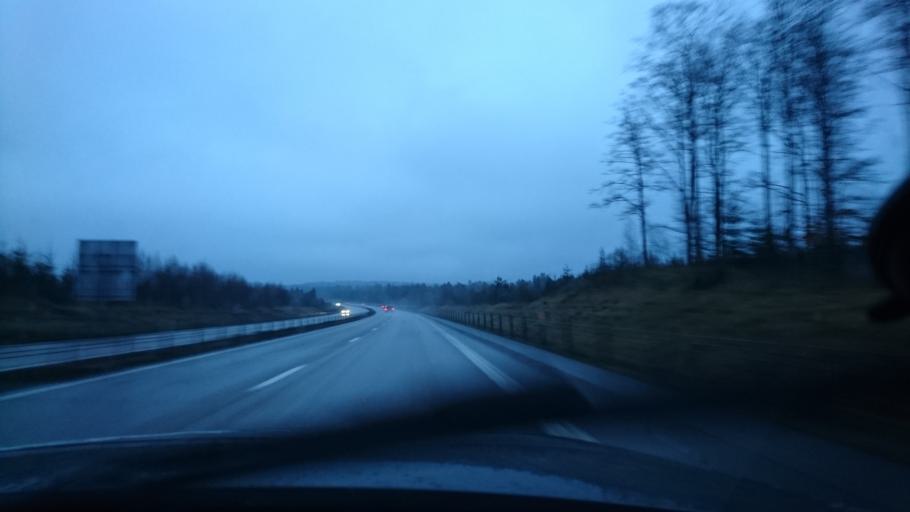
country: SE
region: Skane
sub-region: Orkelljunga Kommun
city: OErkelljunga
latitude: 56.2950
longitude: 13.3752
